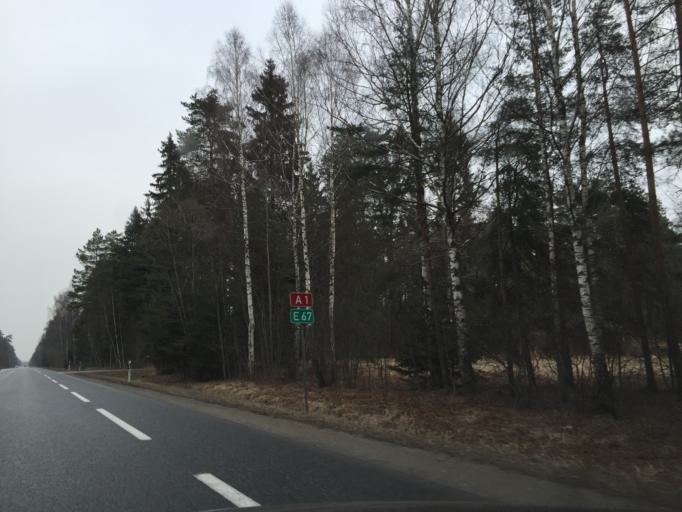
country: LV
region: Saulkrastu
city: Saulkrasti
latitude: 57.4753
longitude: 24.4341
